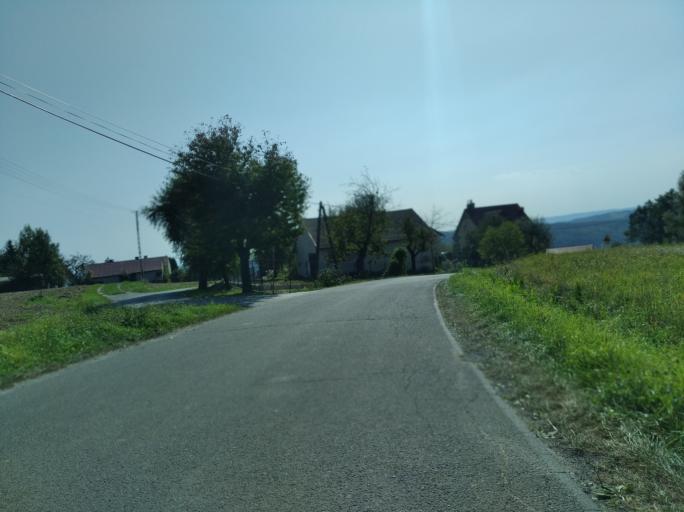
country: PL
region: Subcarpathian Voivodeship
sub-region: Powiat strzyzowski
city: Czudec
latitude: 49.9558
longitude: 21.8315
